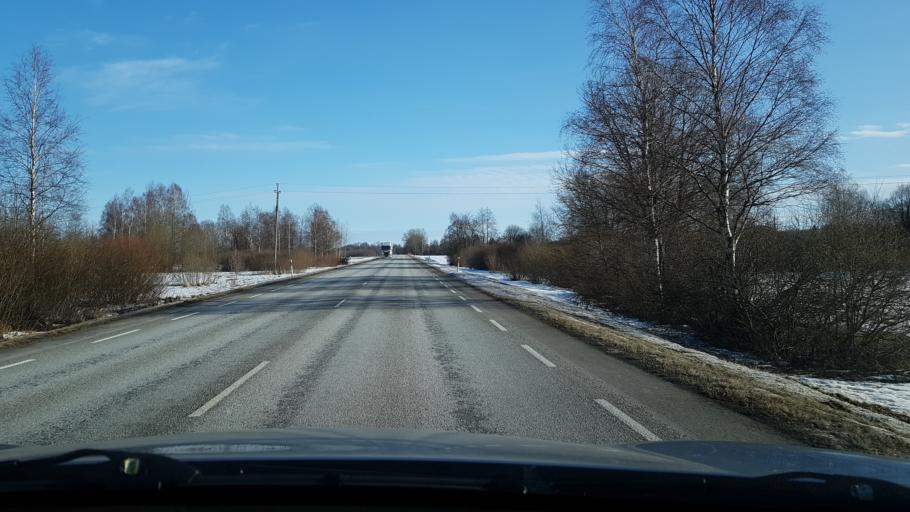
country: EE
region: Viljandimaa
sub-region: Vohma linn
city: Vohma
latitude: 58.6696
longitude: 25.6456
